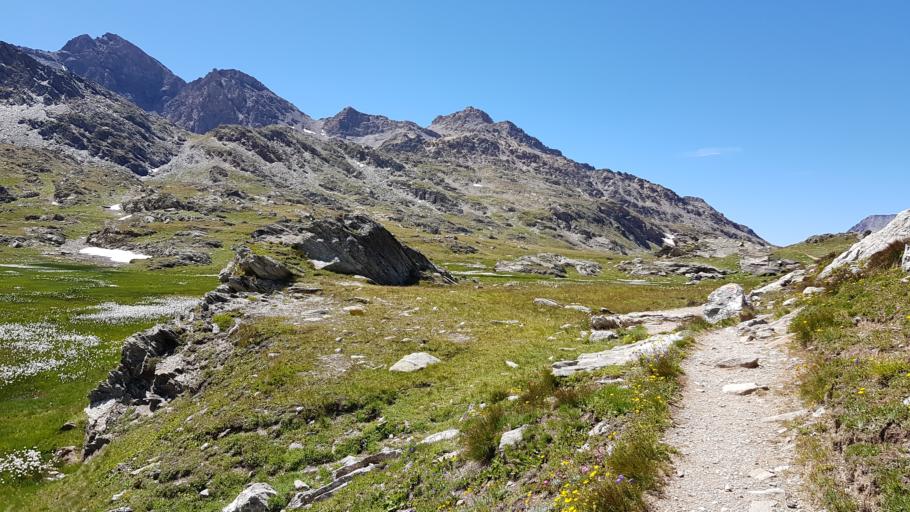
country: IT
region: Piedmont
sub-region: Provincia di Cuneo
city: Pontechianale
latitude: 44.6424
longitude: 6.9543
